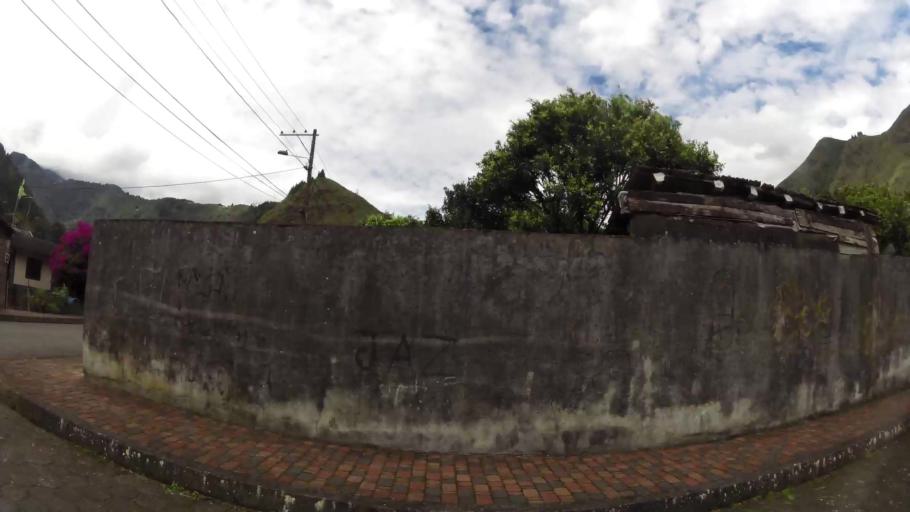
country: EC
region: Tungurahua
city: Banos
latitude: -1.3959
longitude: -78.3965
